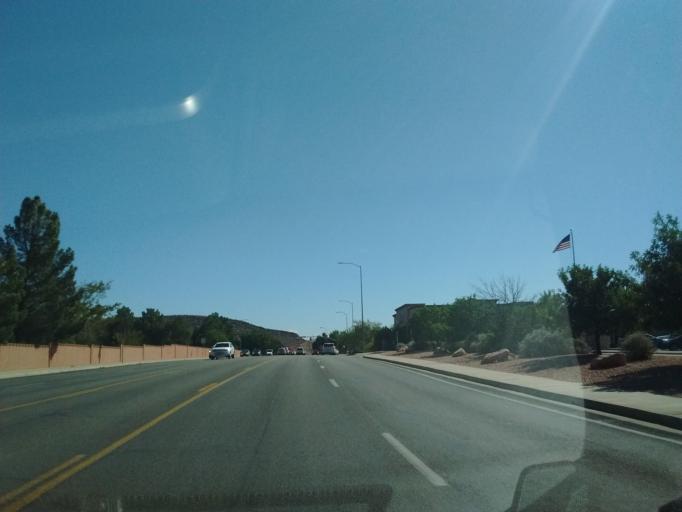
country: US
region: Utah
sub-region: Washington County
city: Saint George
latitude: 37.0887
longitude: -113.5591
